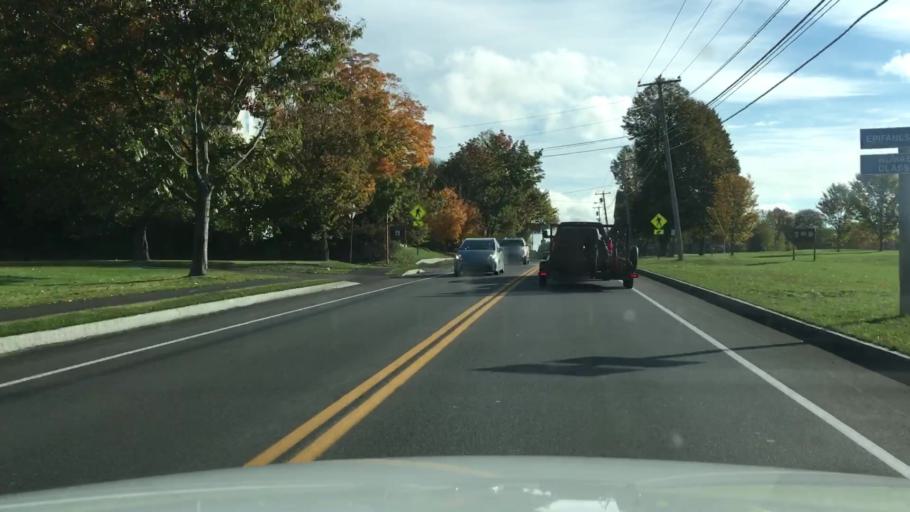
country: US
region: Maine
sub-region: Knox County
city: Thomaston
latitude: 44.0776
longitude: -69.1944
